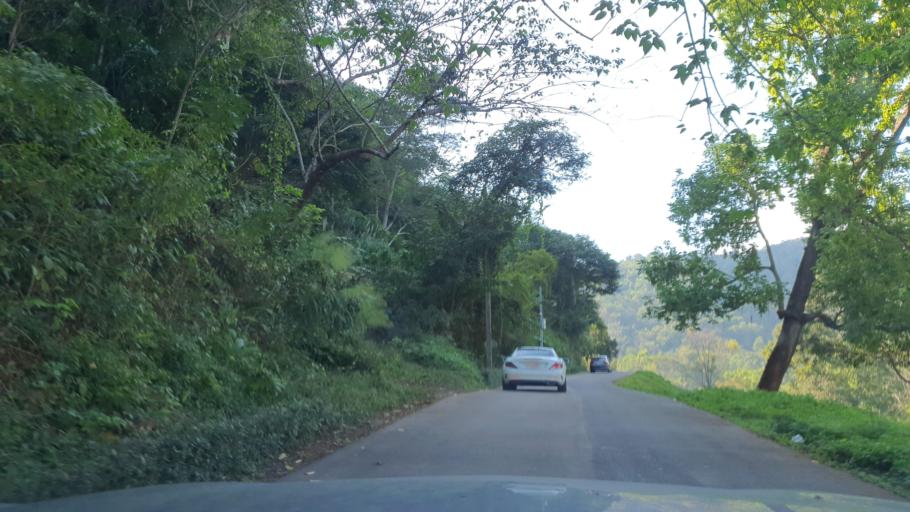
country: TH
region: Chiang Mai
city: Samoeng
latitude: 18.9004
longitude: 98.8259
